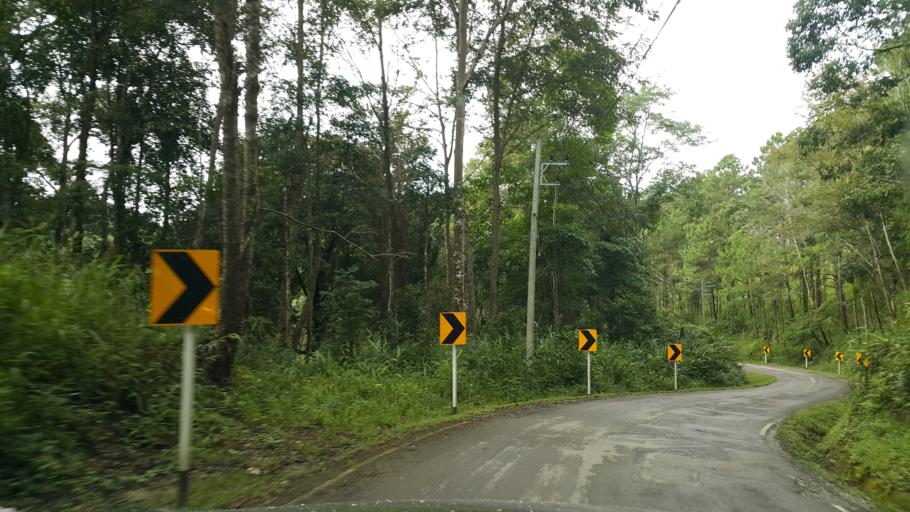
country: TH
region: Chiang Mai
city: Samoeng
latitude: 18.8847
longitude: 98.5031
